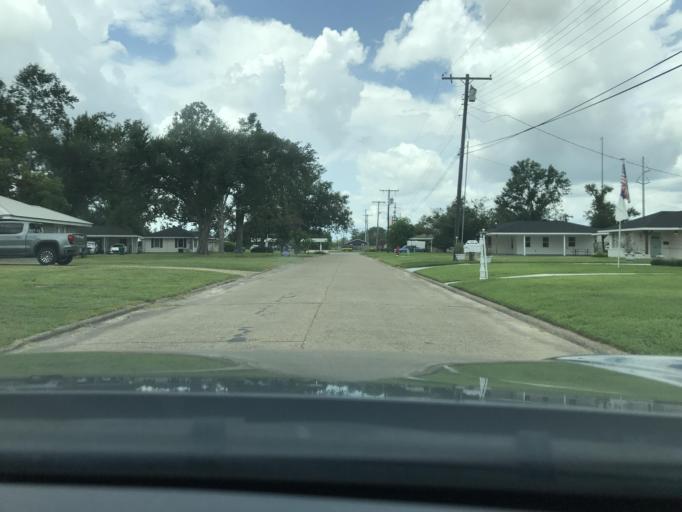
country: US
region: Louisiana
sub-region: Calcasieu Parish
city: Westlake
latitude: 30.2516
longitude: -93.2564
